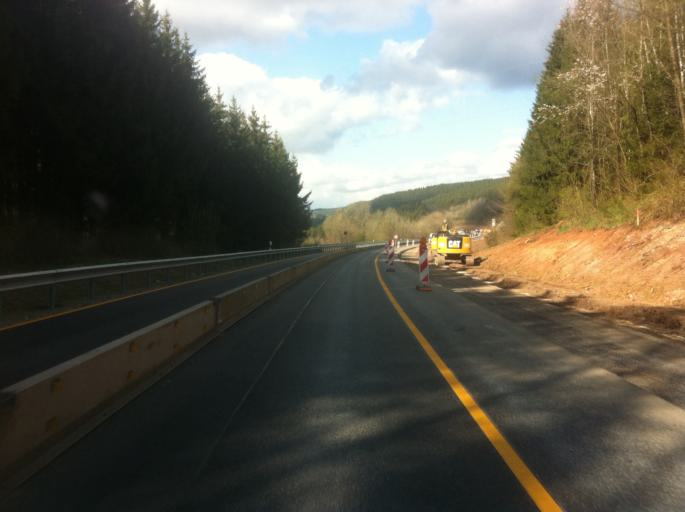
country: DE
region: Rheinland-Pfalz
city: Weinsheim
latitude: 50.2275
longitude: 6.4494
